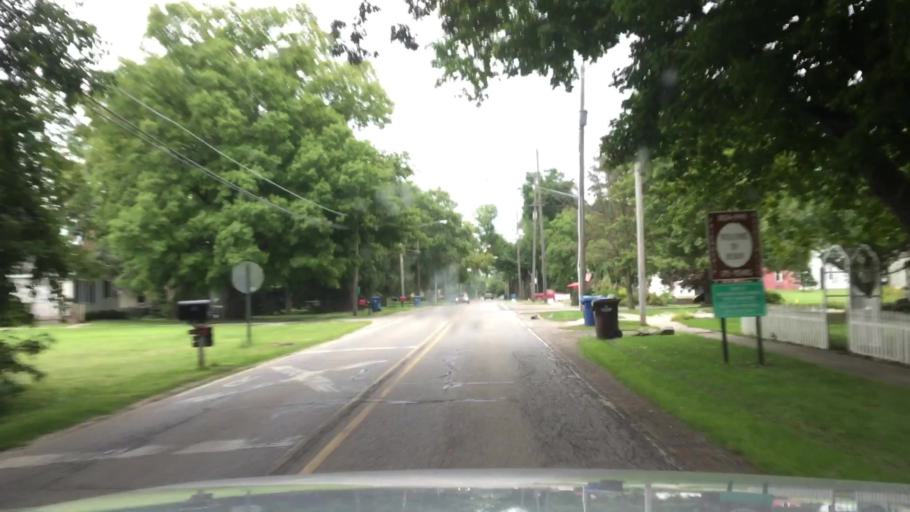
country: US
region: Michigan
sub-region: Shiawassee County
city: Durand
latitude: 42.8238
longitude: -83.9530
